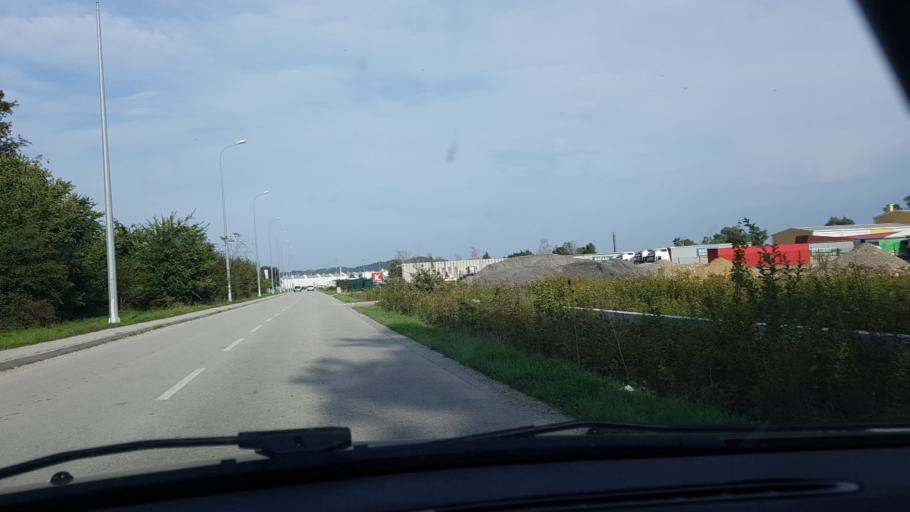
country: HR
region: Krapinsko-Zagorska
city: Zabok
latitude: 46.0163
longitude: 15.8876
